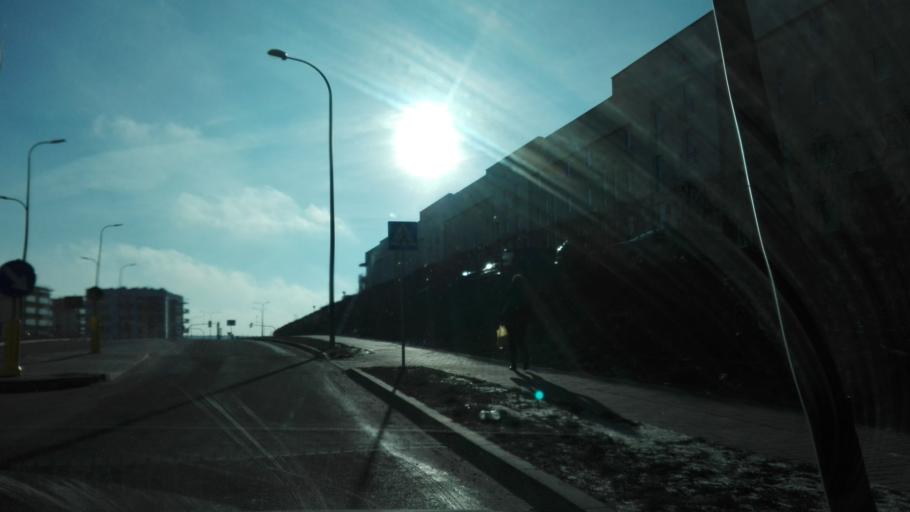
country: PL
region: Lublin Voivodeship
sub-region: Powiat lubelski
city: Kozubszczyzna
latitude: 51.2248
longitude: 22.4921
